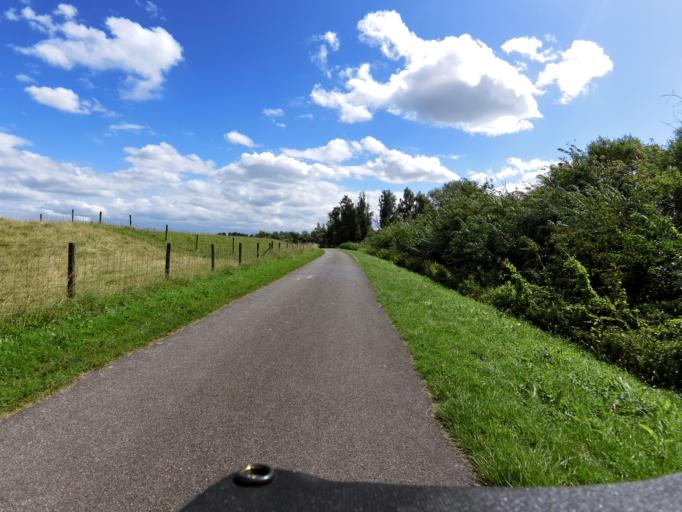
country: NL
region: South Holland
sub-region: Gemeente Zwijndrecht
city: Heerjansdam
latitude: 51.8187
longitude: 4.5640
